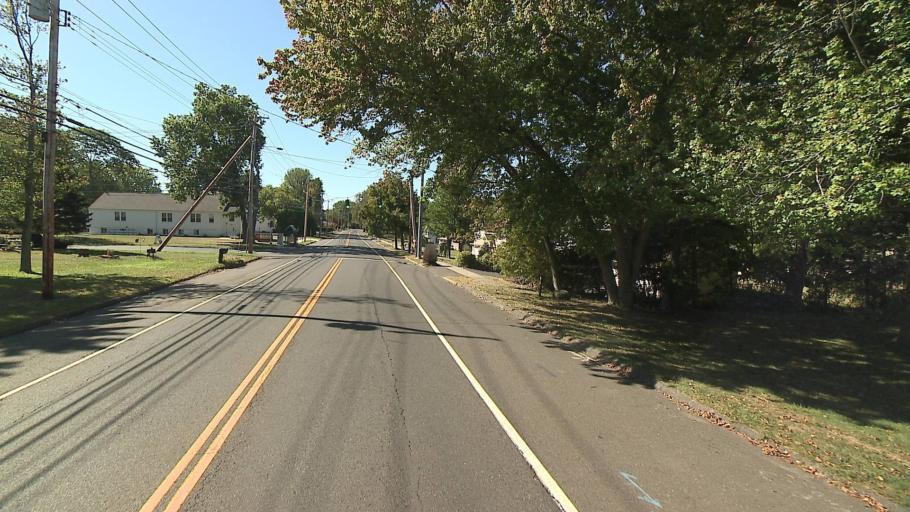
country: US
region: Connecticut
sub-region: New Haven County
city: Woodmont
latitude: 41.2443
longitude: -72.9812
